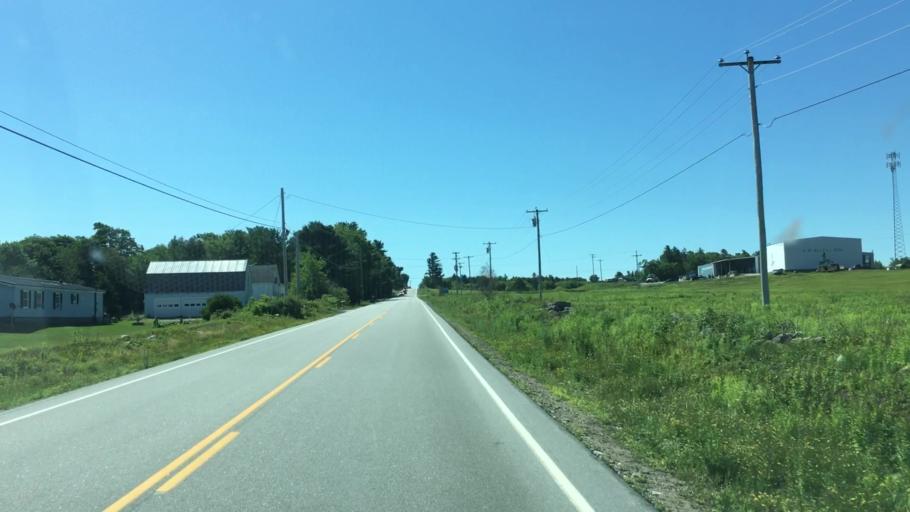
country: US
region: Maine
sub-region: Hancock County
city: Orland
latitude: 44.5518
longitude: -68.6929
